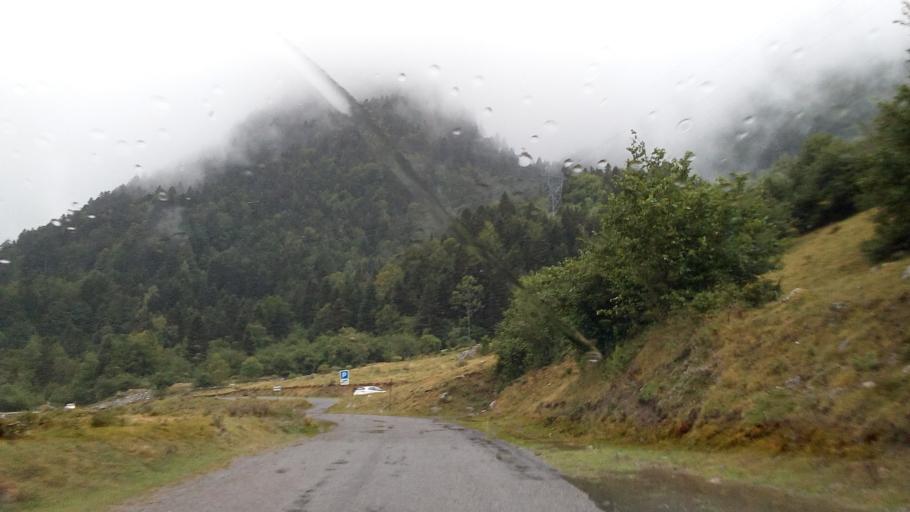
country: FR
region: Midi-Pyrenees
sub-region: Departement des Hautes-Pyrenees
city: Cauterets
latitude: 42.9144
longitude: -0.2584
